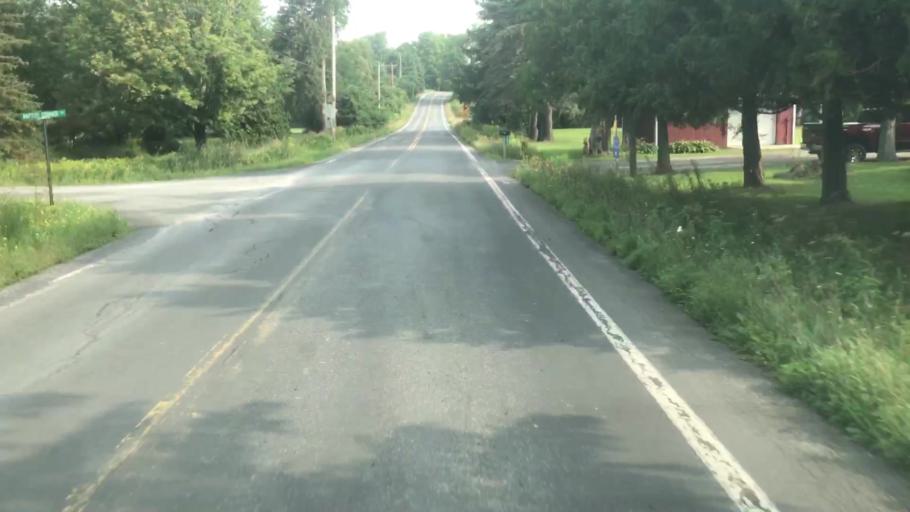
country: US
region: New York
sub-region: Onondaga County
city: Skaneateles
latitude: 42.9011
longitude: -76.4534
